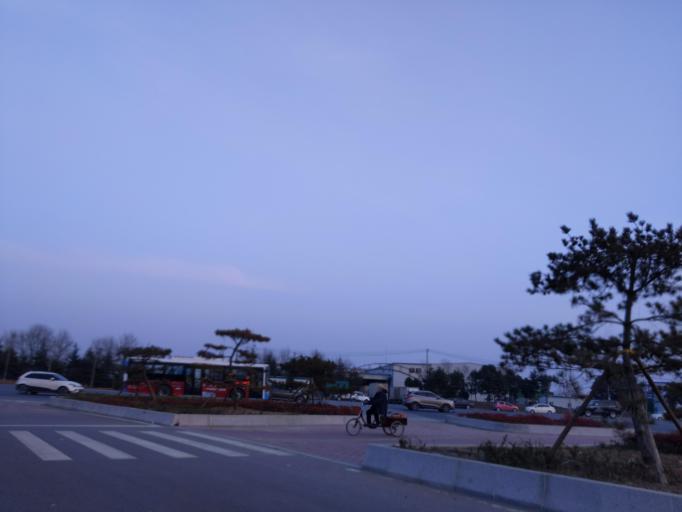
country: CN
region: Henan Sheng
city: Zhongyuanlu
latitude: 35.8123
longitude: 115.0659
